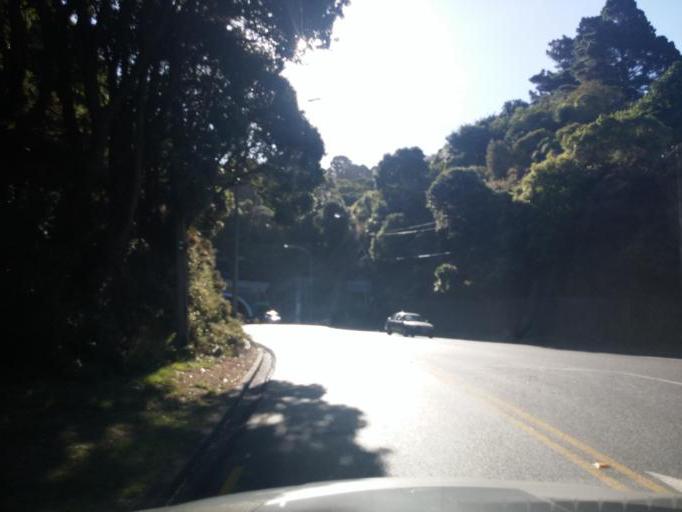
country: NZ
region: Wellington
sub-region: Wellington City
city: Wellington
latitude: -41.3046
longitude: 174.7924
